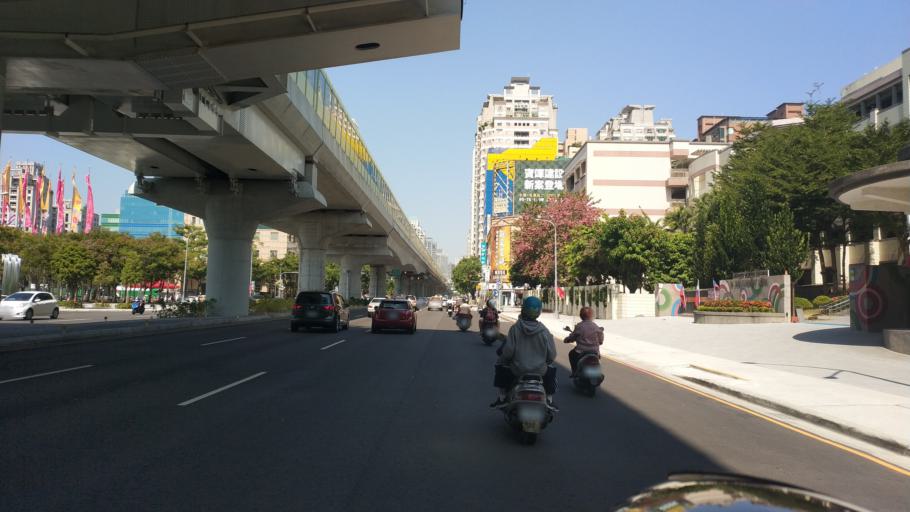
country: TW
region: Taiwan
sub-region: Taichung City
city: Taichung
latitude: 24.1456
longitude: 120.6468
